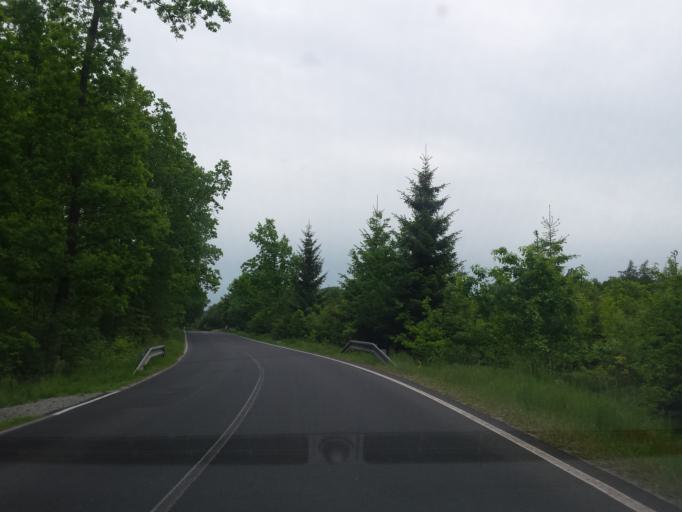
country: CZ
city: Novy Bor
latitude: 50.7491
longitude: 14.5706
